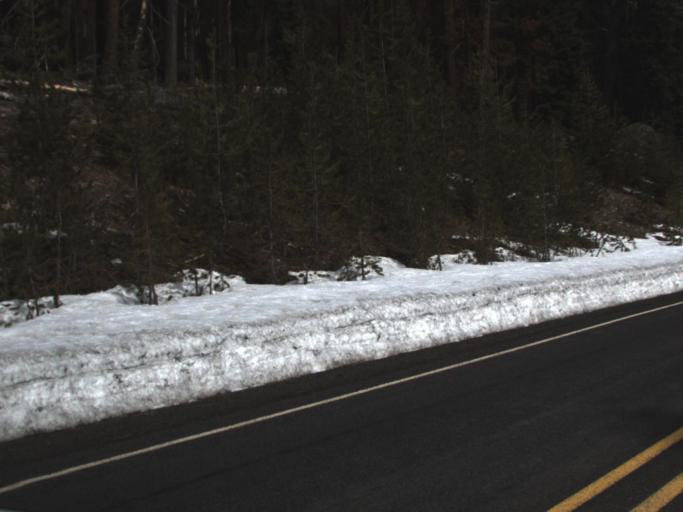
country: US
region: Washington
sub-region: Kittitas County
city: Cle Elum
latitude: 46.9368
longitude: -121.3485
